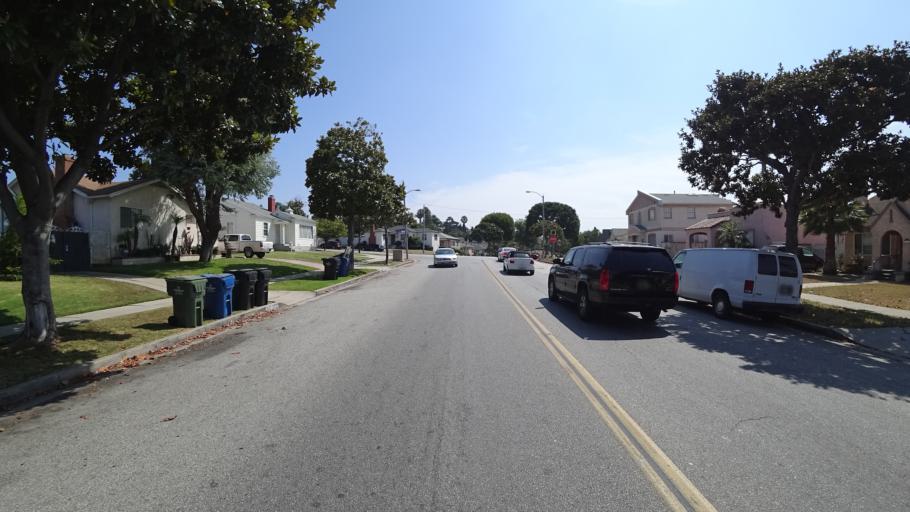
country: US
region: California
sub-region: Los Angeles County
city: View Park-Windsor Hills
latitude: 33.9801
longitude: -118.3556
